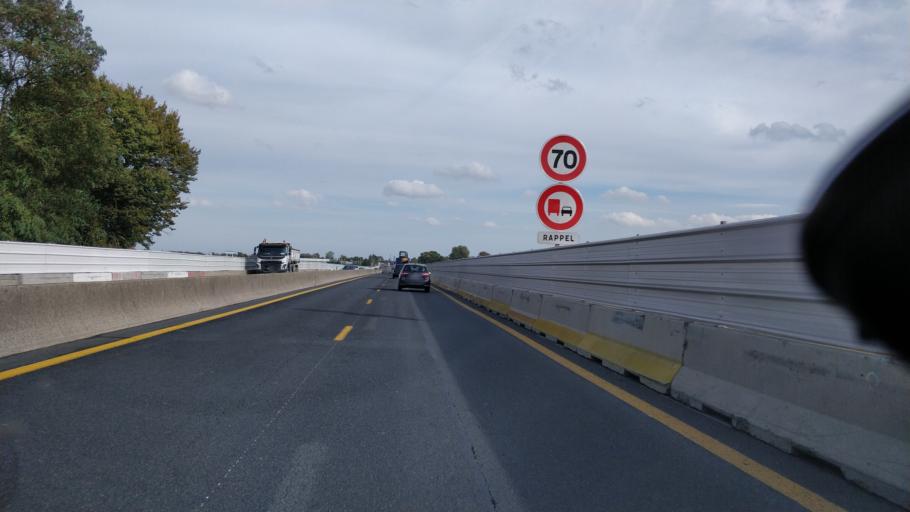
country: FR
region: Ile-de-France
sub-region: Departement de Seine-et-Marne
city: Villevaude
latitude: 48.9424
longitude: 2.6502
